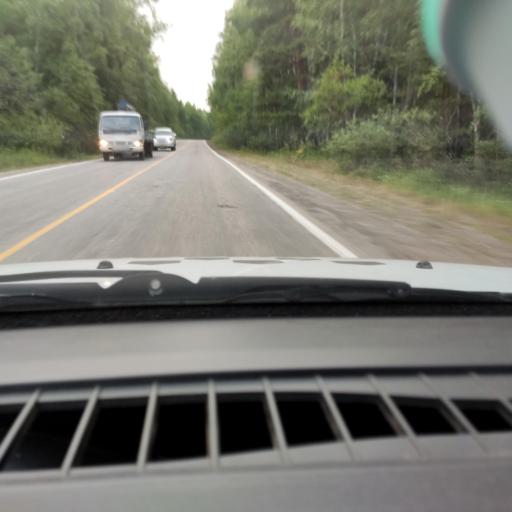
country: RU
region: Chelyabinsk
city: Ozersk
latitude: 55.8327
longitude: 60.6481
